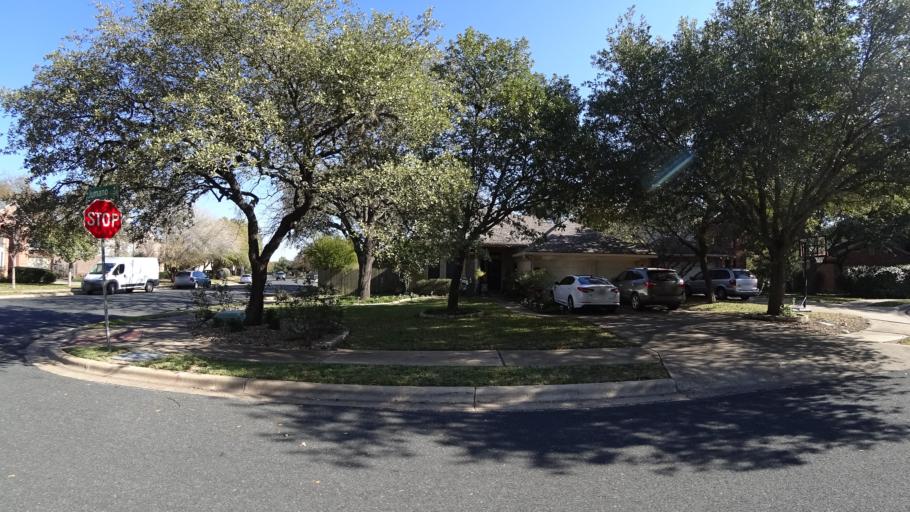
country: US
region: Texas
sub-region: Travis County
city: Barton Creek
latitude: 30.2263
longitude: -97.8656
